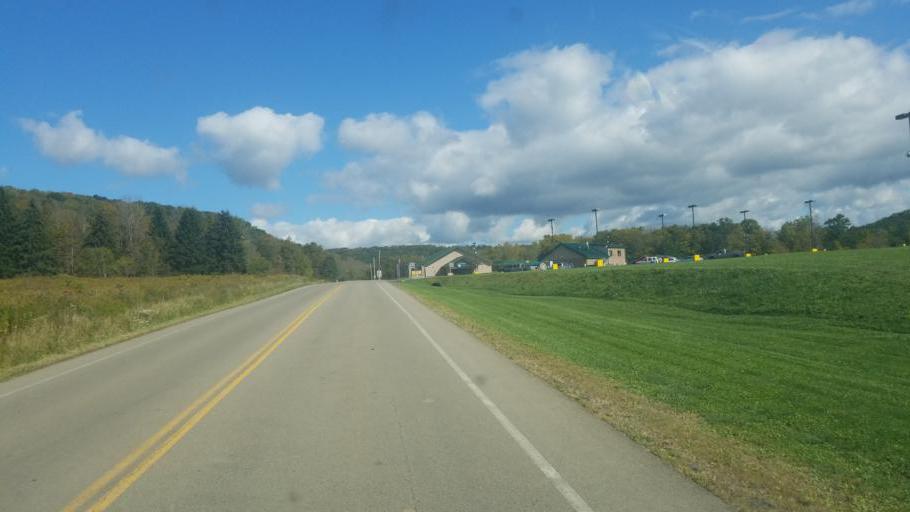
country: US
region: New York
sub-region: Allegany County
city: Cuba
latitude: 42.2342
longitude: -78.3112
